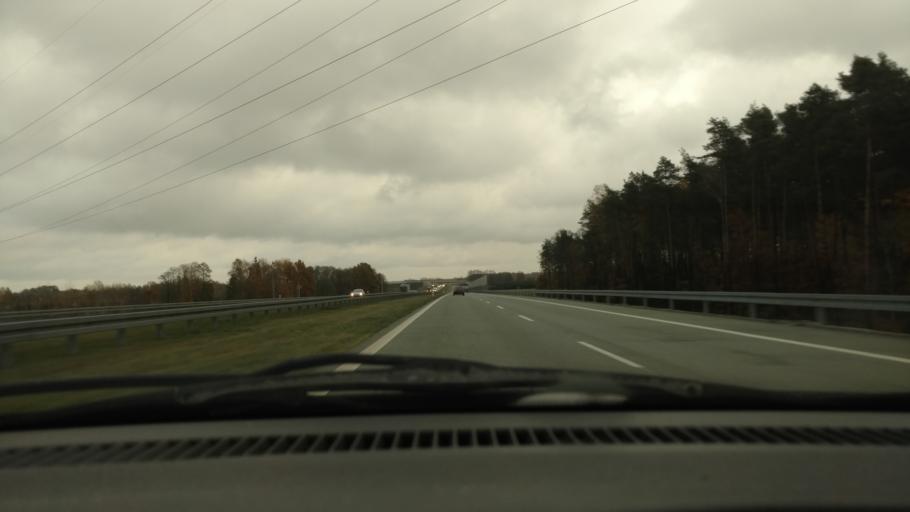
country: PL
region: Lodz Voivodeship
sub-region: Powiat pabianicki
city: Pabianice
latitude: 51.6078
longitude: 19.3241
